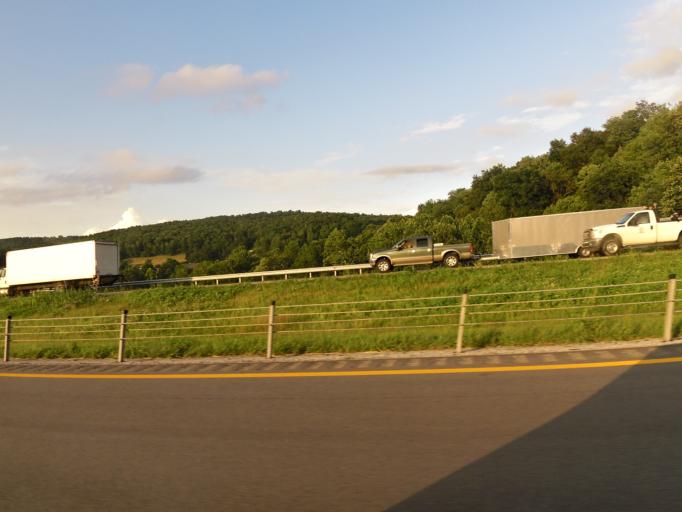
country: US
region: Kentucky
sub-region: Rockcastle County
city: Mount Vernon
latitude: 37.3834
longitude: -84.3352
